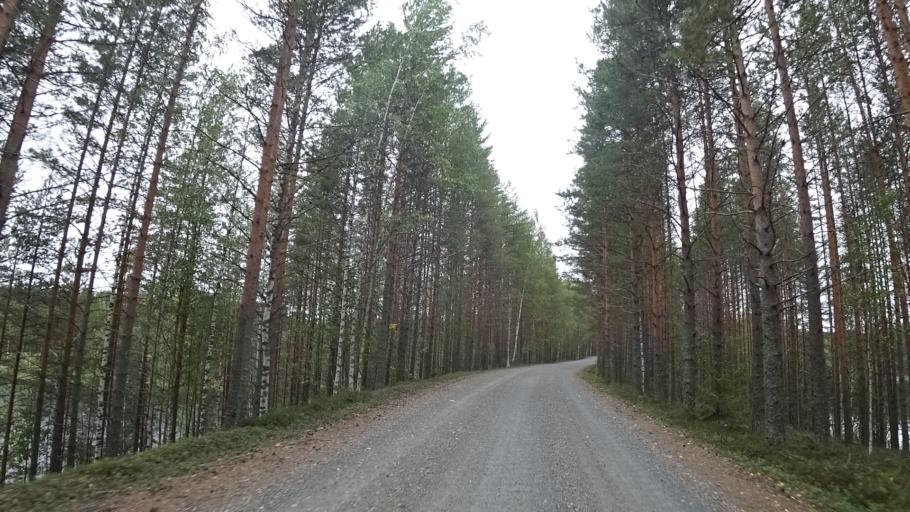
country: FI
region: North Karelia
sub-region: Joensuu
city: Ilomantsi
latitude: 62.6185
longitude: 31.1946
